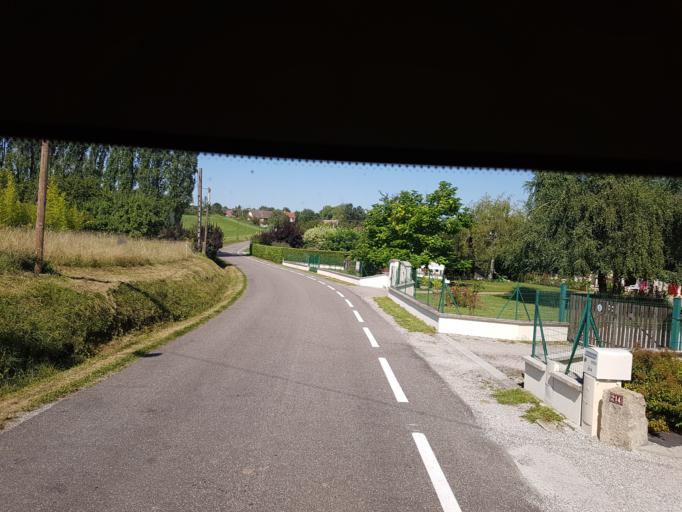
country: FR
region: Franche-Comte
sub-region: Departement du Jura
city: Perrigny
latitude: 46.7299
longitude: 5.5802
